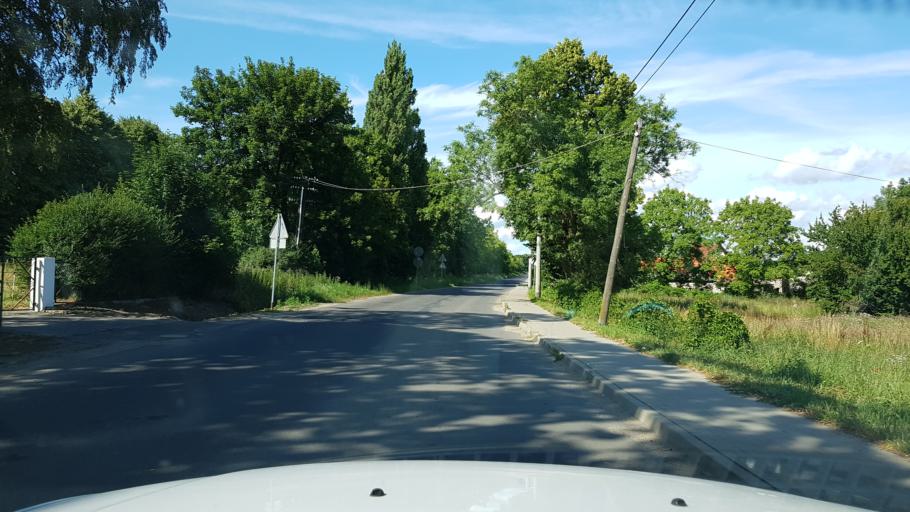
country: PL
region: West Pomeranian Voivodeship
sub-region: Powiat gryfinski
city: Stare Czarnowo
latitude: 53.2858
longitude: 14.7813
